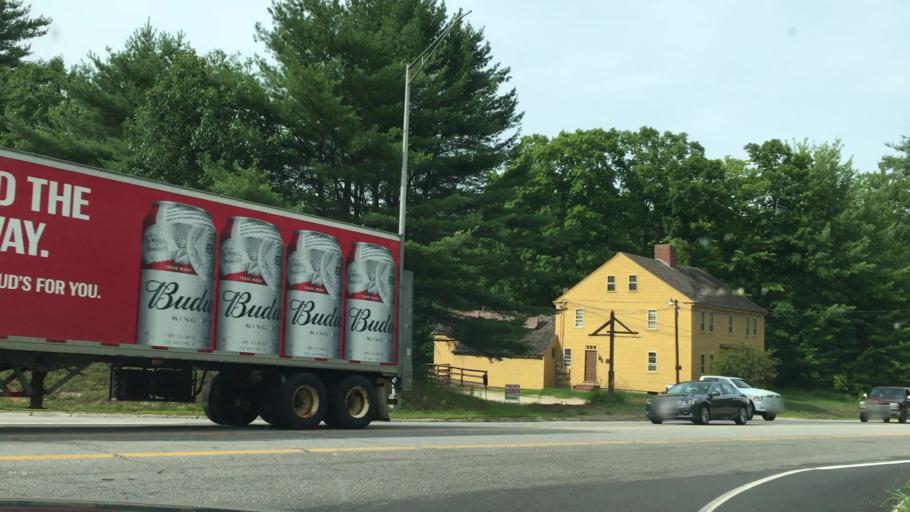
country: US
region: New Hampshire
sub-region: Grafton County
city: Ashland
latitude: 43.6140
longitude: -71.6412
